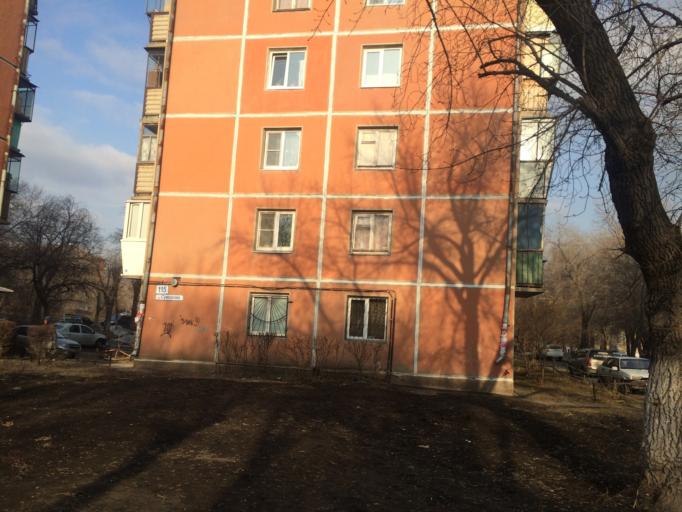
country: RU
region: Chelyabinsk
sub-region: Gorod Magnitogorsk
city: Magnitogorsk
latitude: 53.4027
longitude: 58.9717
